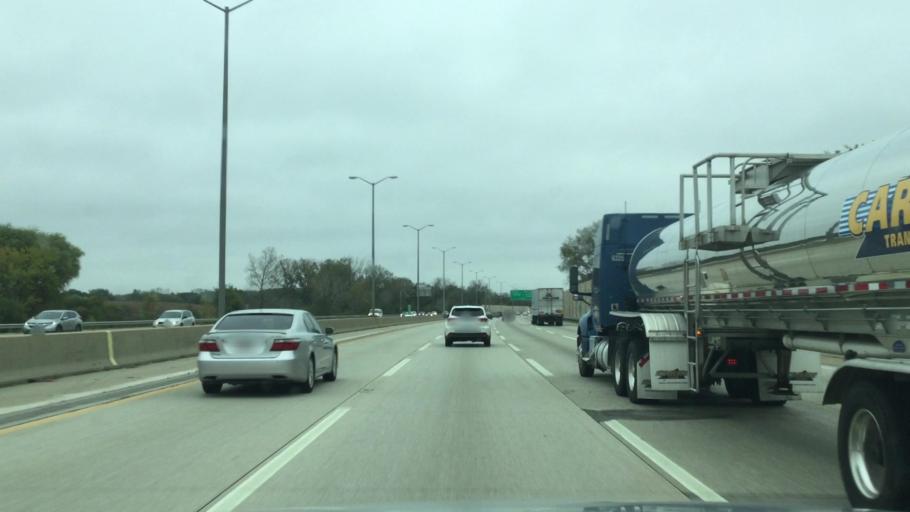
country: US
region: Illinois
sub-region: Lake County
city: Bannockburn
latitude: 42.1865
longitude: -87.8786
